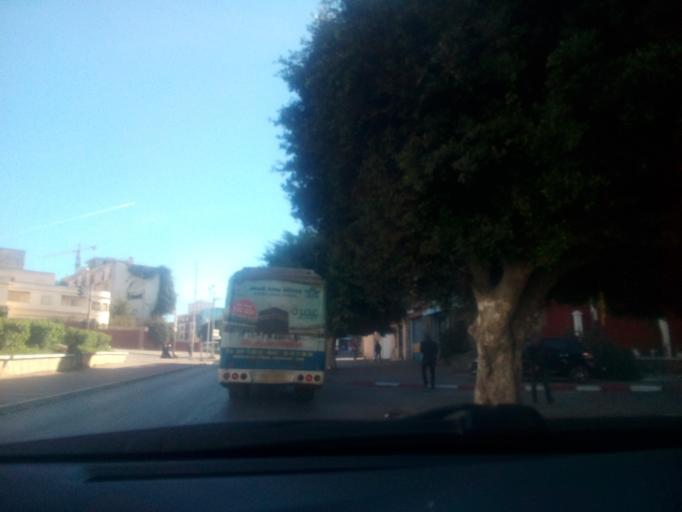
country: DZ
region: Oran
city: Oran
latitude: 35.7057
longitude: -0.6113
